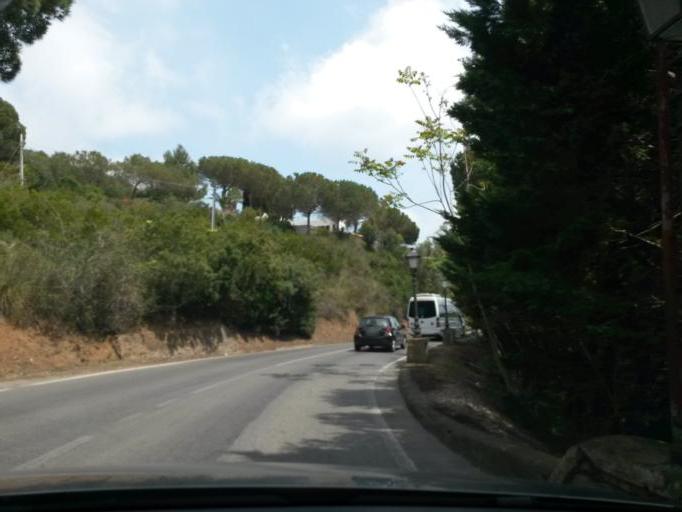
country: IT
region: Tuscany
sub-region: Provincia di Livorno
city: Porto Azzurro
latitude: 42.7618
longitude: 10.3872
